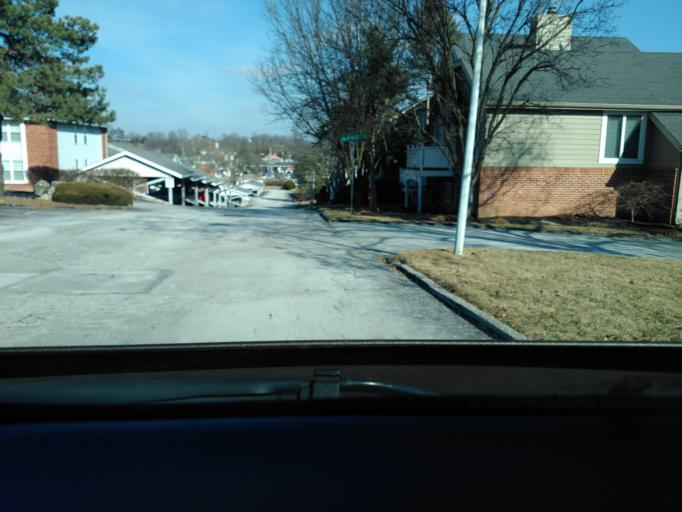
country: US
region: Missouri
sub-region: Saint Louis County
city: Manchester
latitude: 38.6237
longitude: -90.5203
